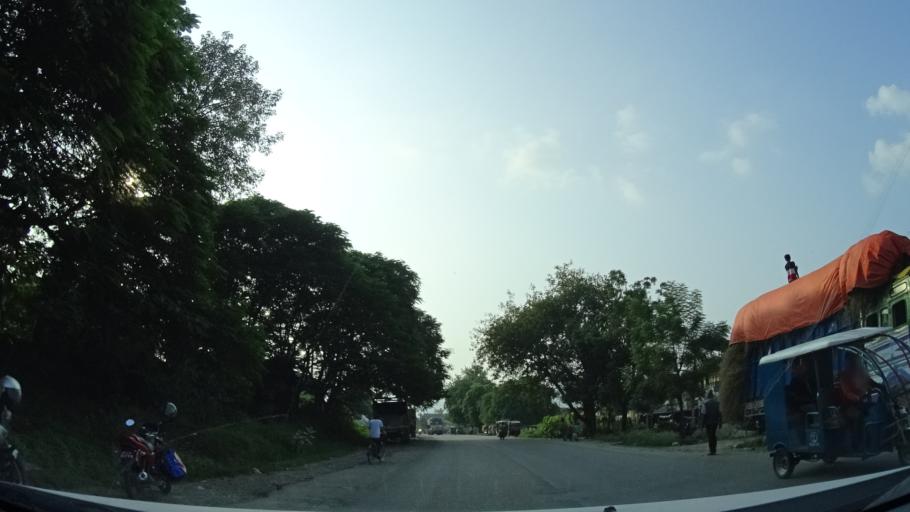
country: NP
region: Central Region
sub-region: Narayani Zone
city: Bharatpur
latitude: 27.7039
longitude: 84.4147
